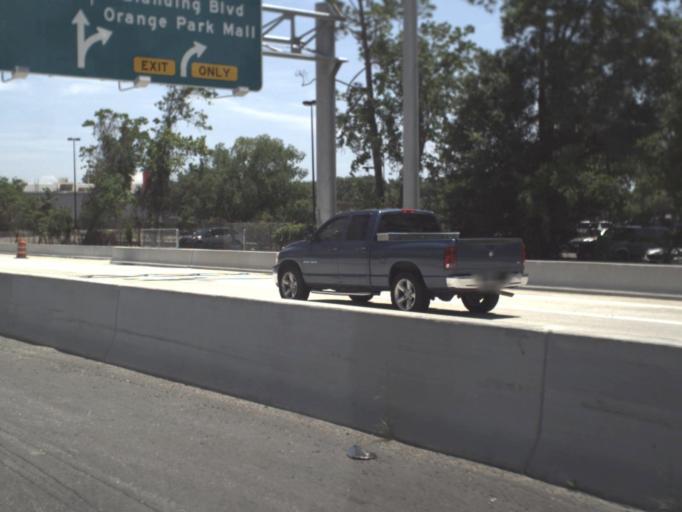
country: US
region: Florida
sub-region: Clay County
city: Bellair-Meadowbrook Terrace
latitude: 30.1986
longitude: -81.7450
